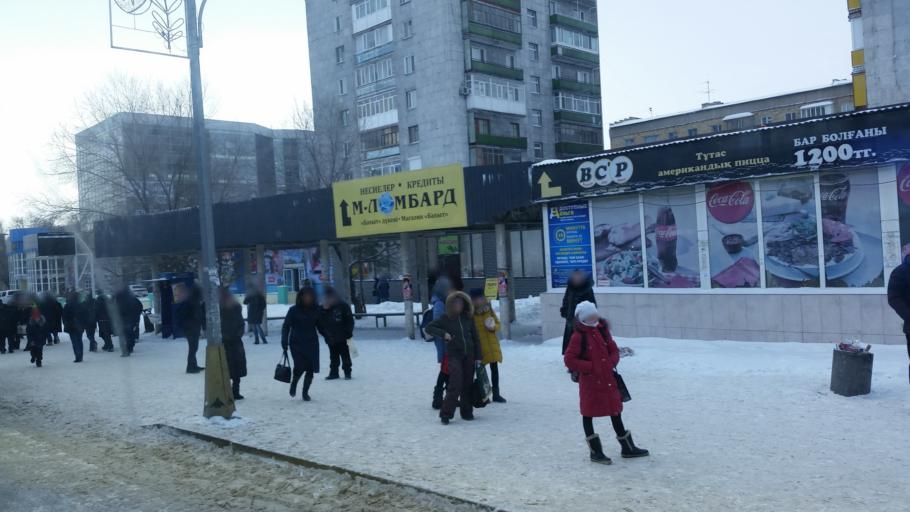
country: KZ
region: Qaraghandy
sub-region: Qaraghandy Qalasy
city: Karagandy
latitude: 49.7989
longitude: 73.0903
